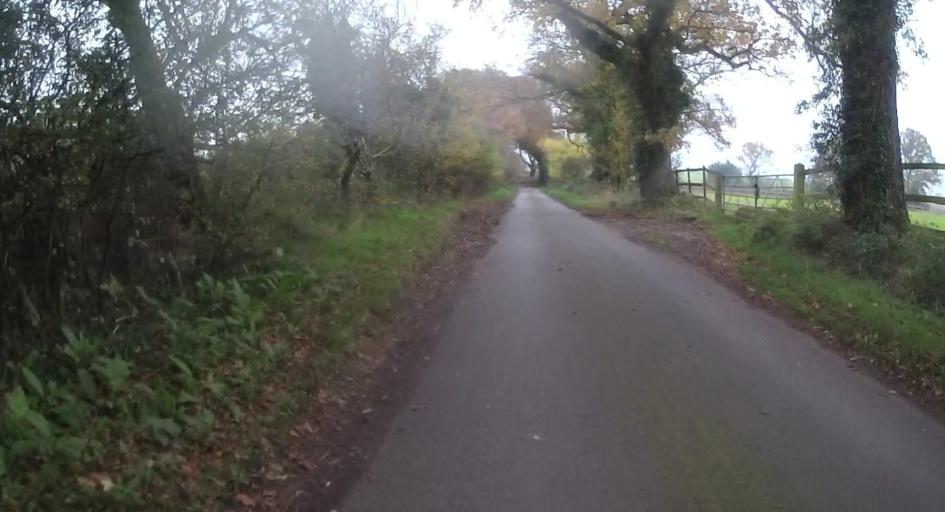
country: GB
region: England
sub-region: Wokingham
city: Finchampstead
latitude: 51.3723
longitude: -0.8756
